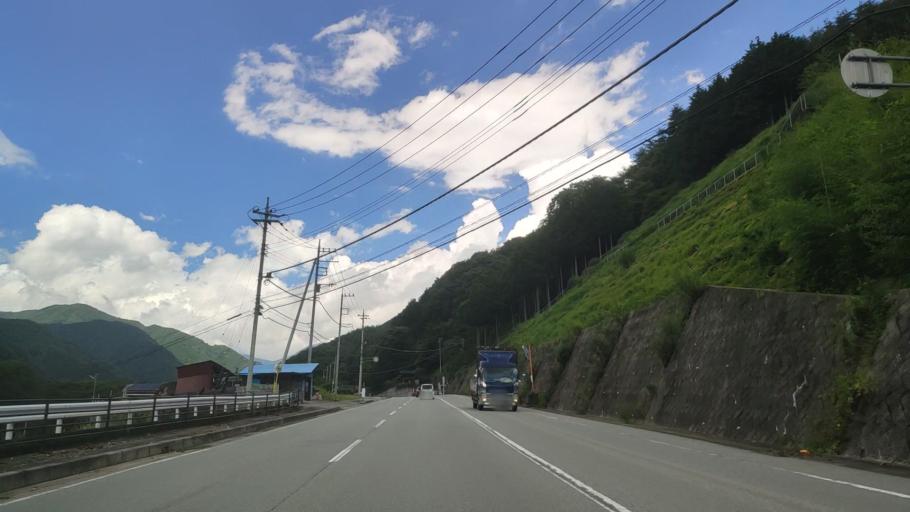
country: JP
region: Yamanashi
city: Enzan
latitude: 35.8015
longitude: 138.7491
